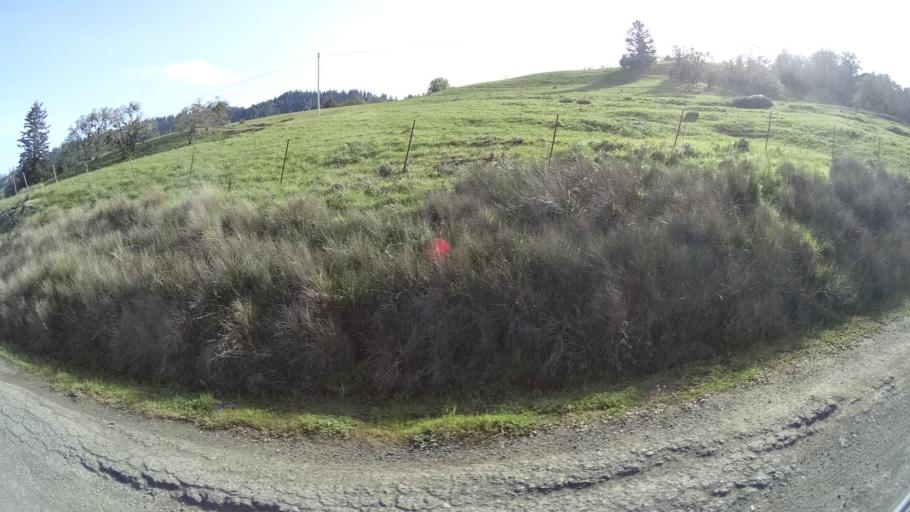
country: US
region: California
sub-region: Humboldt County
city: Hydesville
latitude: 40.6585
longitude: -123.9266
